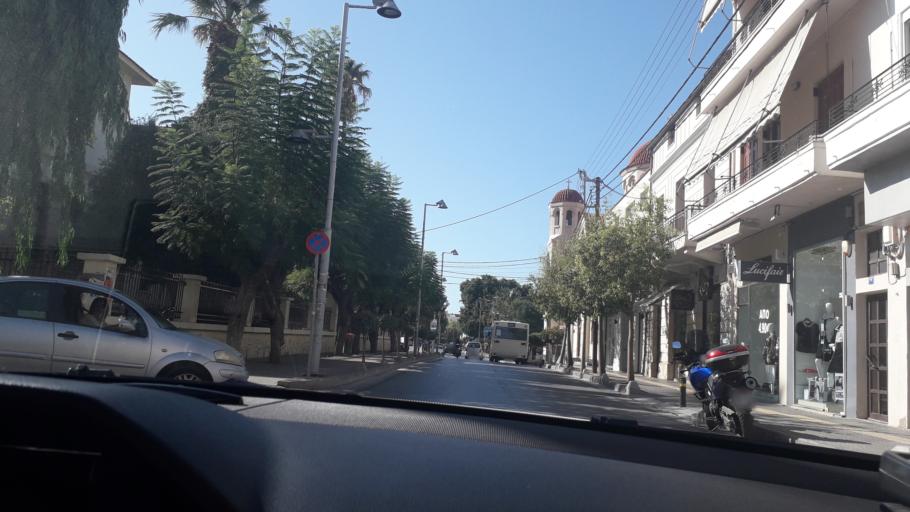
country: GR
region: Crete
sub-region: Nomos Rethymnis
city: Rethymno
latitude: 35.3665
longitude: 24.4759
